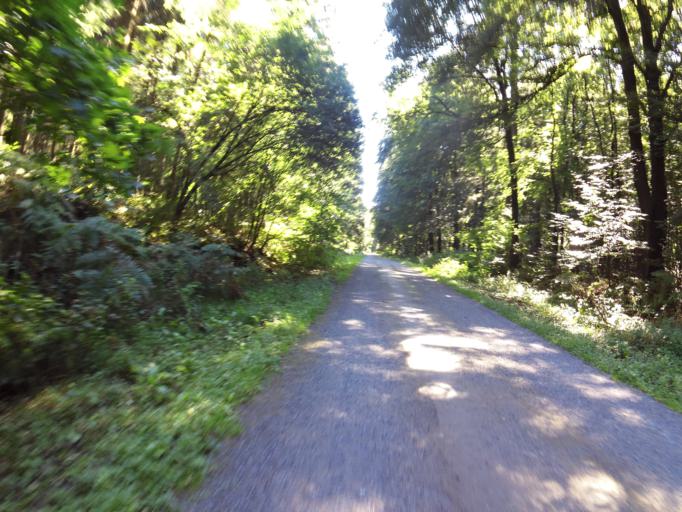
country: NL
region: Gelderland
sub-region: Gemeente Groesbeek
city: De Horst
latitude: 51.7454
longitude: 5.9859
